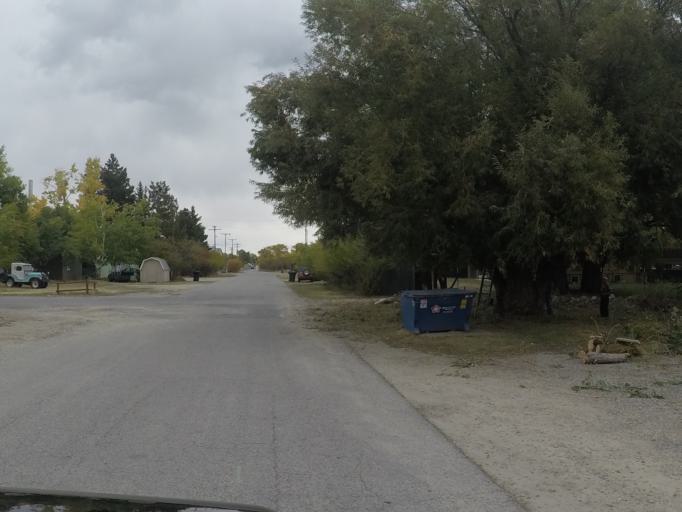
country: US
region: Montana
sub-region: Carbon County
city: Red Lodge
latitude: 45.1946
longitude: -109.2446
